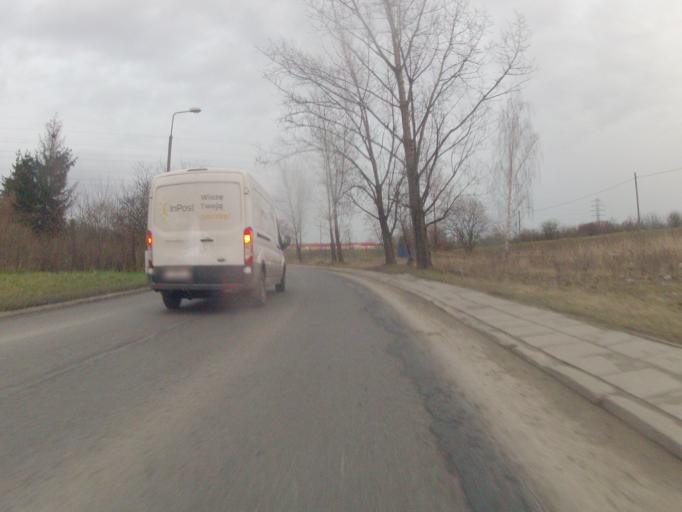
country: PL
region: Lesser Poland Voivodeship
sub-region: Krakow
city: Krakow
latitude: 50.0503
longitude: 20.0052
